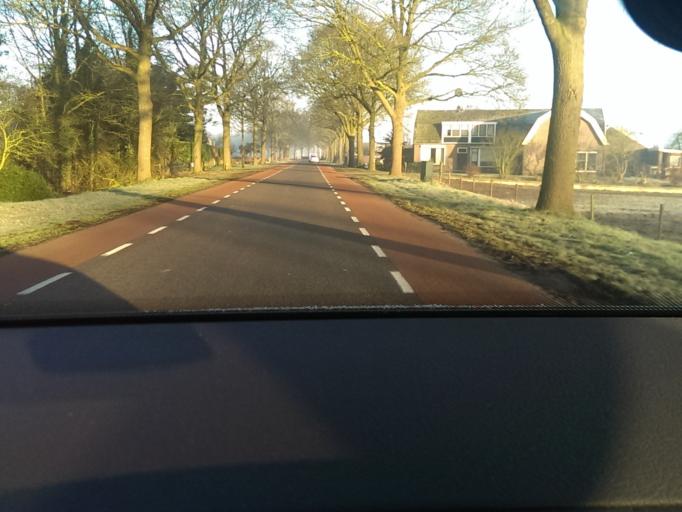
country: NL
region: Overijssel
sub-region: Gemeente Wierden
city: Wierden
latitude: 52.4049
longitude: 6.5714
